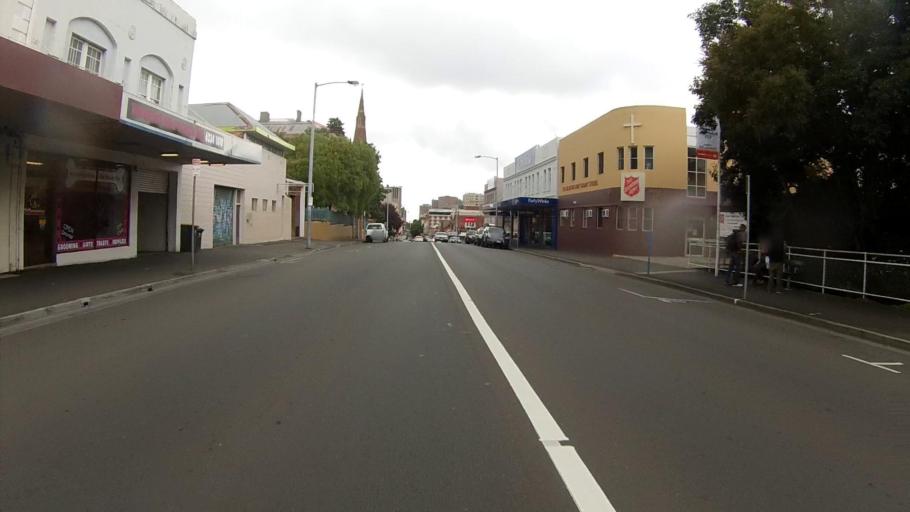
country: AU
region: Tasmania
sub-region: Hobart
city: Hobart
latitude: -42.8789
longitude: 147.3219
